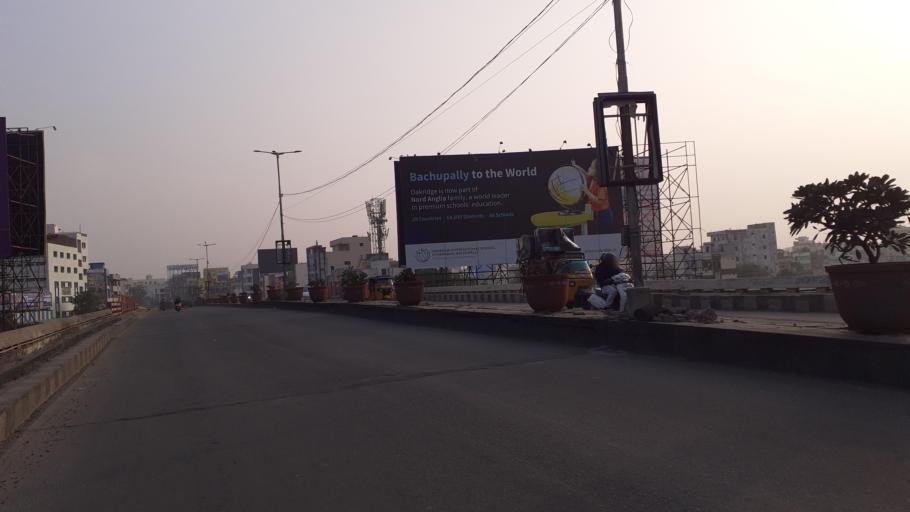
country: IN
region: Telangana
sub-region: Rangareddi
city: Kukatpalli
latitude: 17.4835
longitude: 78.3605
